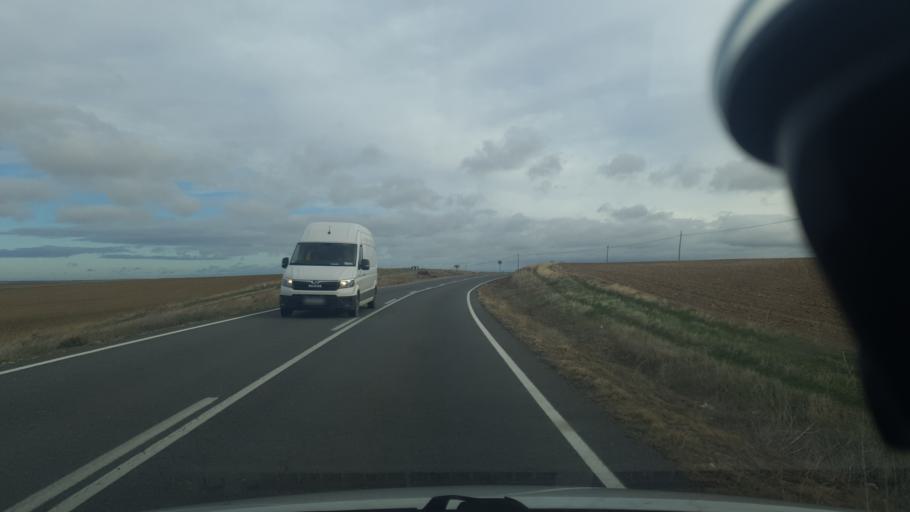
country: ES
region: Castille and Leon
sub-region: Provincia de Avila
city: Gotarrendura
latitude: 40.8175
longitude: -4.7508
